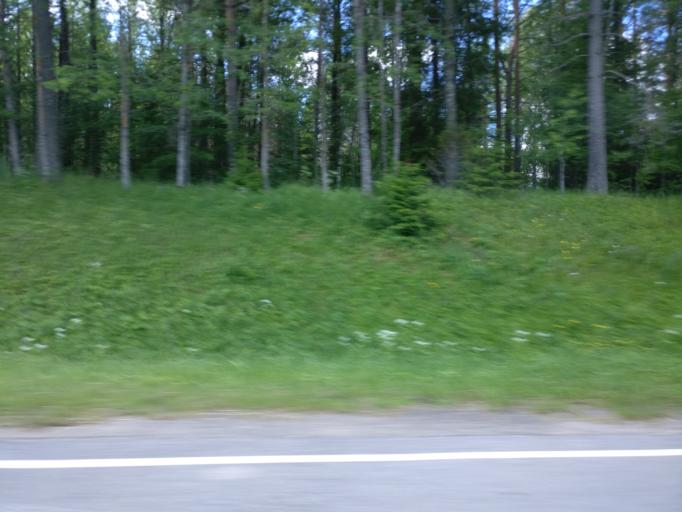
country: FI
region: Southern Savonia
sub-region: Savonlinna
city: Kerimaeki
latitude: 61.8730
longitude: 29.1206
